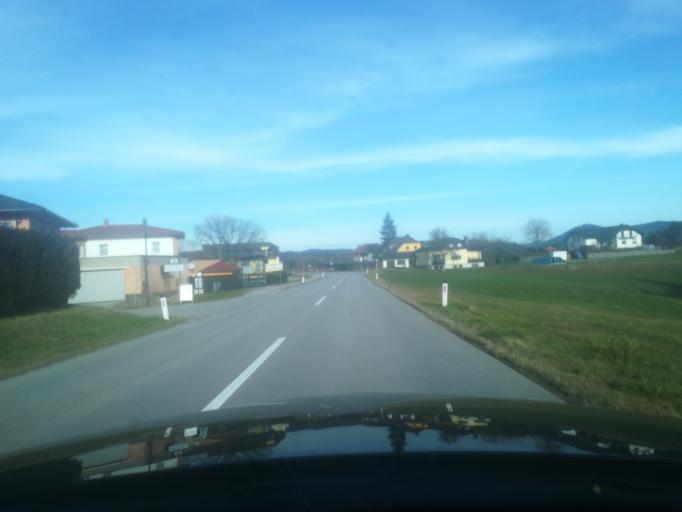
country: AT
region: Upper Austria
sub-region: Politischer Bezirk Perg
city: Perg
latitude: 48.3126
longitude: 14.6621
